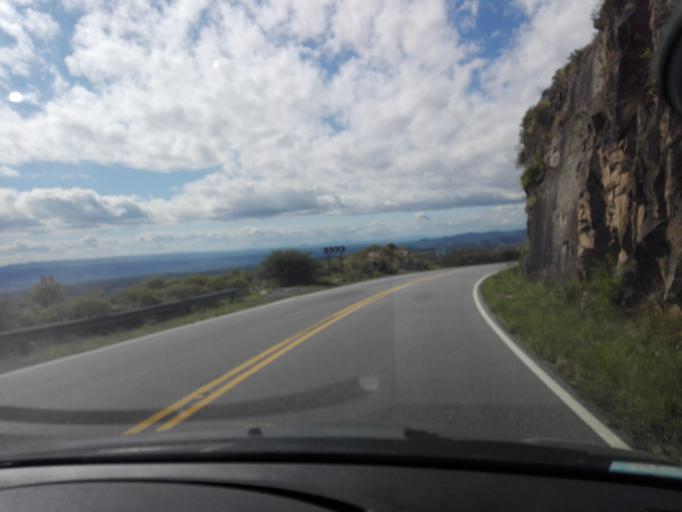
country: AR
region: Cordoba
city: Mina Clavero
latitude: -31.7699
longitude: -64.9193
